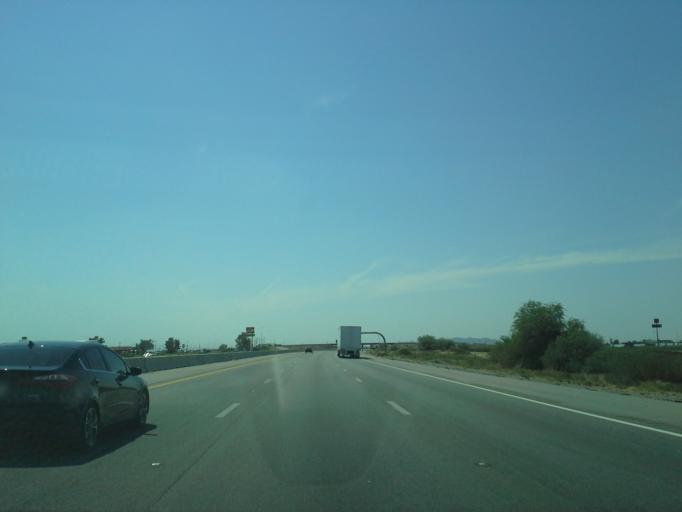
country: US
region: Arizona
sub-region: Pinal County
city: Eloy
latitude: 32.7323
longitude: -111.5415
